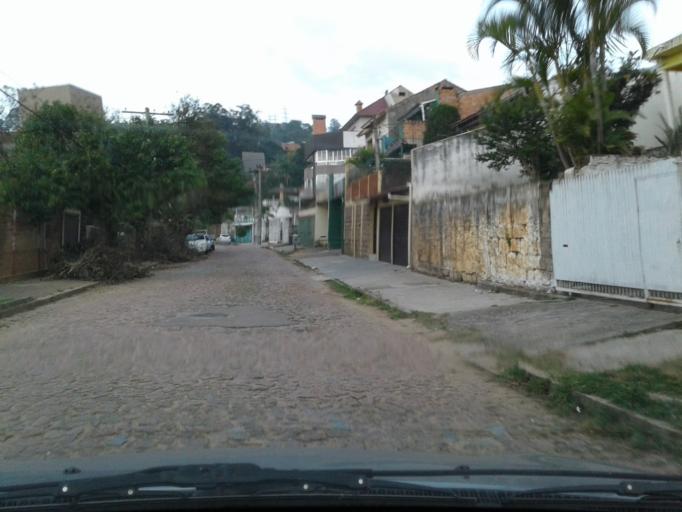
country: BR
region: Rio Grande do Sul
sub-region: Porto Alegre
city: Porto Alegre
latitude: -30.0638
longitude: -51.1488
